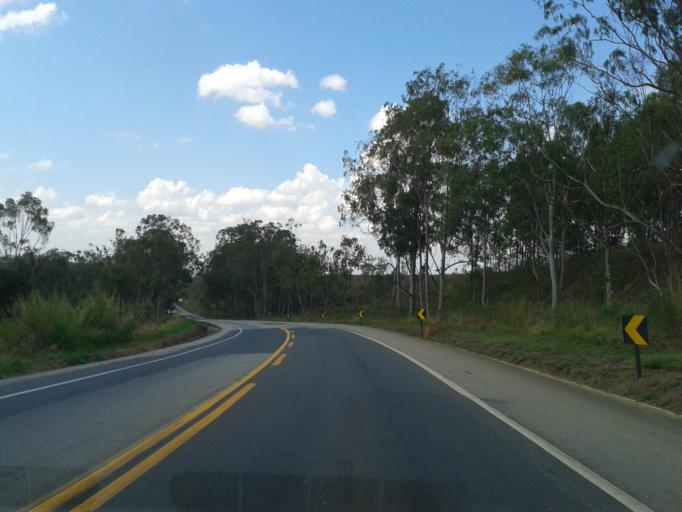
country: BR
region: Minas Gerais
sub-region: Campos Altos
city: Campos Altos
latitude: -19.7151
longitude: -45.9284
